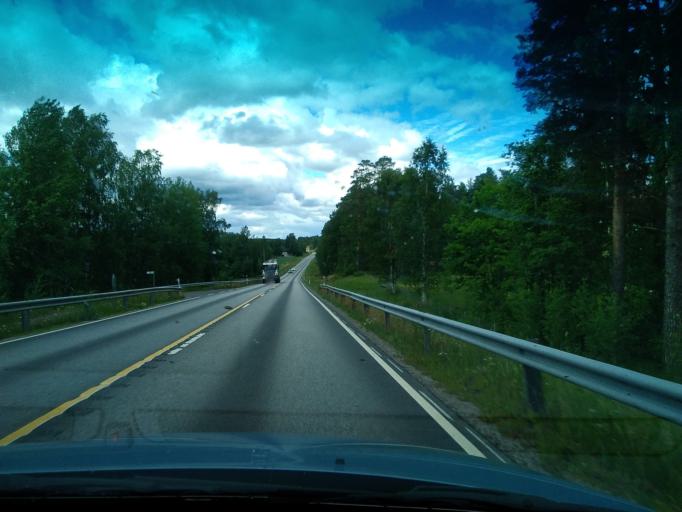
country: FI
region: Central Finland
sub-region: Saarijaervi-Viitasaari
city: Saarijaervi
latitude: 62.8052
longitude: 25.0476
